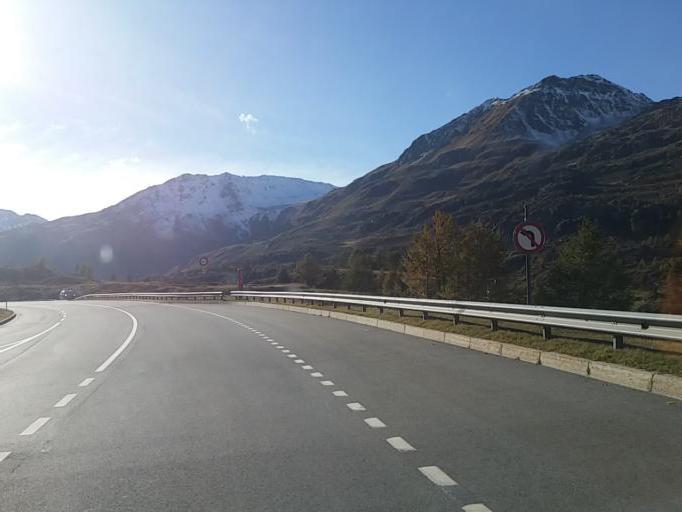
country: CH
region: Valais
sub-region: Brig District
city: Brig
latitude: 46.2512
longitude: 8.0339
